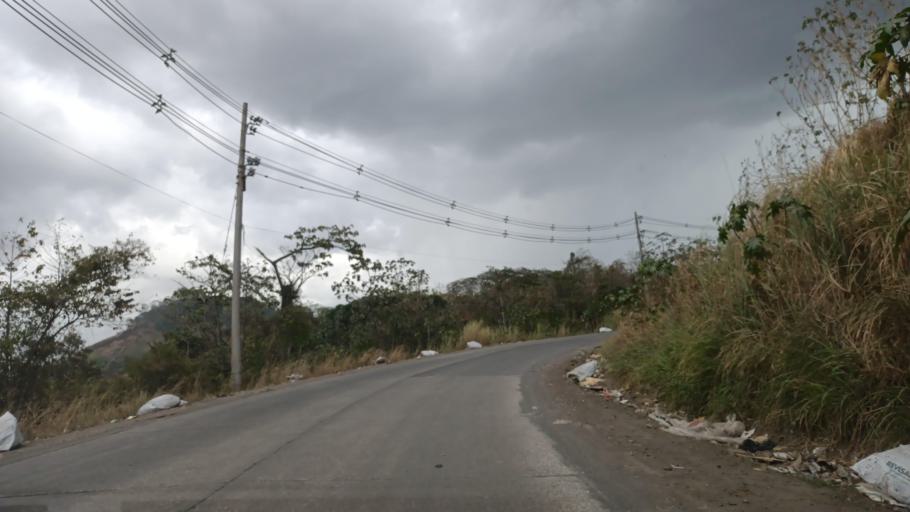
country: PA
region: Panama
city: Las Cumbres
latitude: 9.0532
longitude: -79.5627
